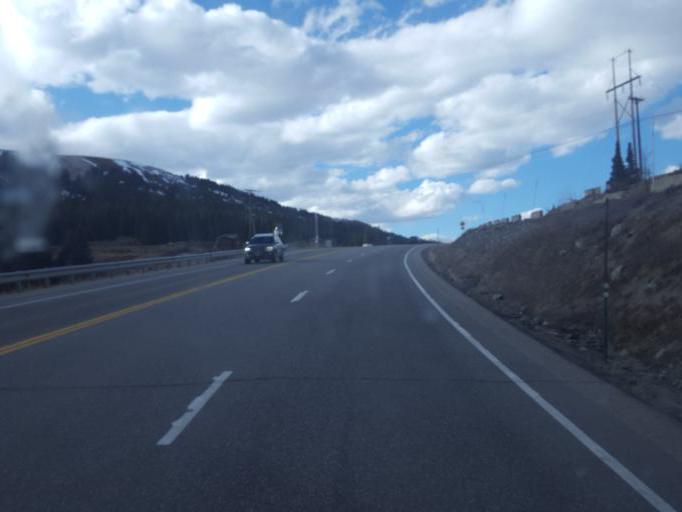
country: US
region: Colorado
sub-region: Lake County
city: Leadville
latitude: 39.3660
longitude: -106.1855
